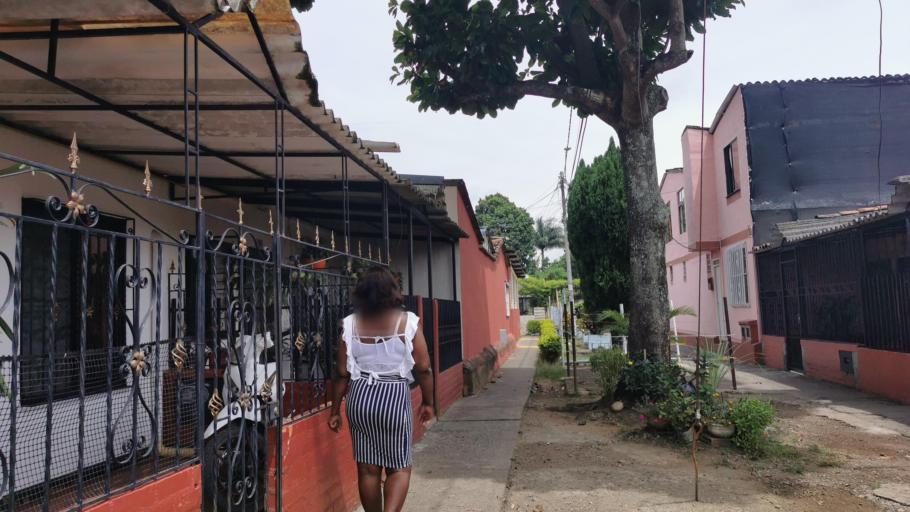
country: CO
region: Valle del Cauca
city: Jamundi
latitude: 3.2539
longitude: -76.5359
